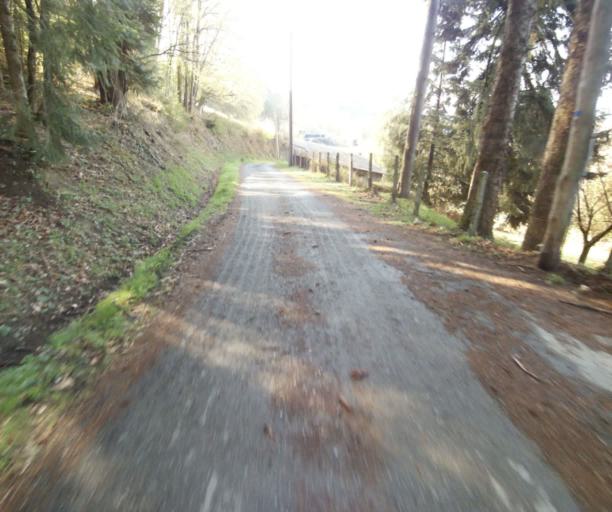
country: FR
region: Limousin
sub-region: Departement de la Correze
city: Laguenne
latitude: 45.2780
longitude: 1.8480
